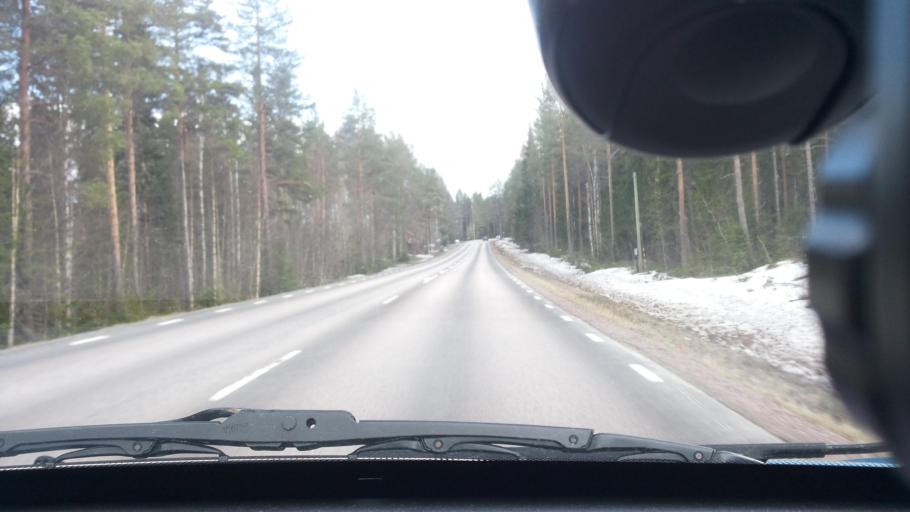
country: SE
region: Norrbotten
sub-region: Lulea Kommun
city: Gammelstad
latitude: 65.5958
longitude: 21.9958
